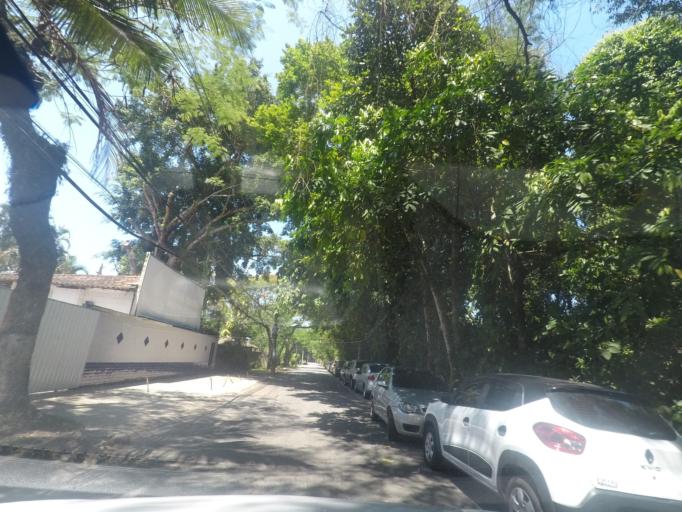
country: BR
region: Rio de Janeiro
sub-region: Nilopolis
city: Nilopolis
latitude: -22.9790
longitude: -43.4569
